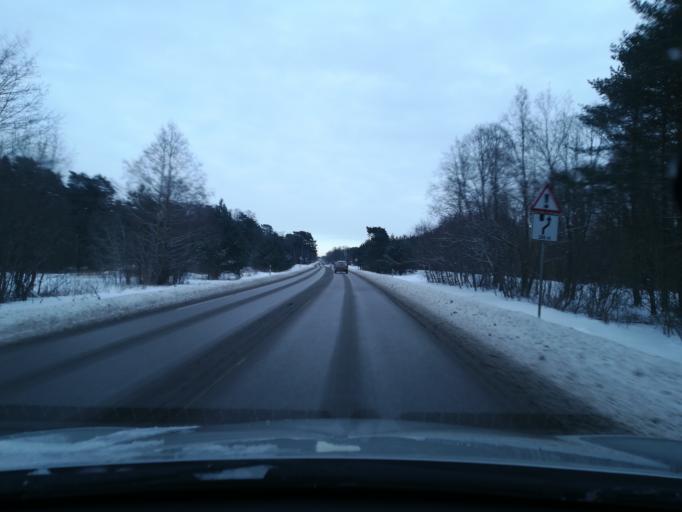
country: EE
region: Harju
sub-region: Harku vald
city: Tabasalu
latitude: 59.4321
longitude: 24.5970
